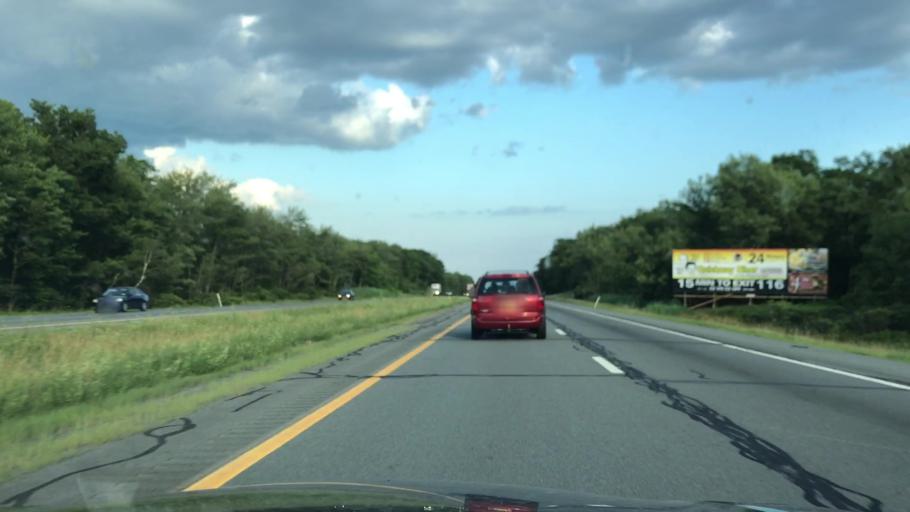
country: US
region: New York
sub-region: Sullivan County
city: Rock Hill
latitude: 41.6006
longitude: -74.5516
